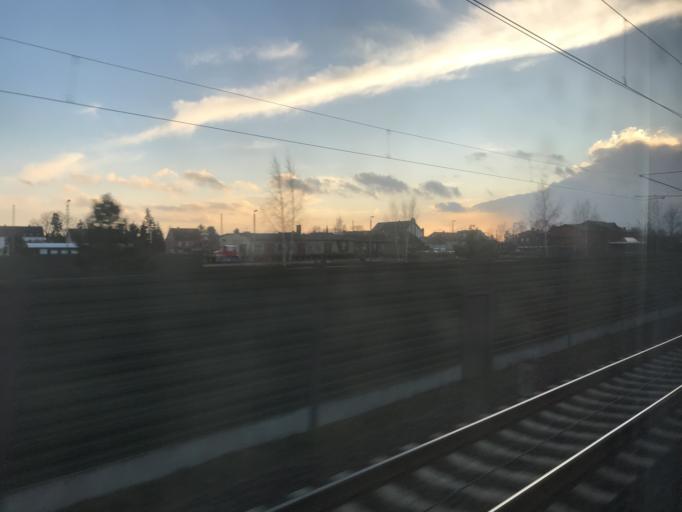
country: DE
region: Saxony-Anhalt
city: Oebisfelde
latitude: 52.4410
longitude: 10.9884
